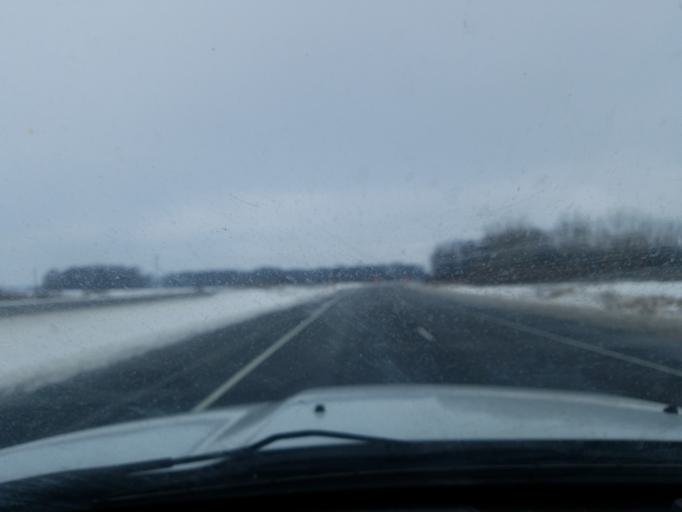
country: US
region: Indiana
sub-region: Marshall County
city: Argos
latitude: 41.2734
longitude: -86.2706
